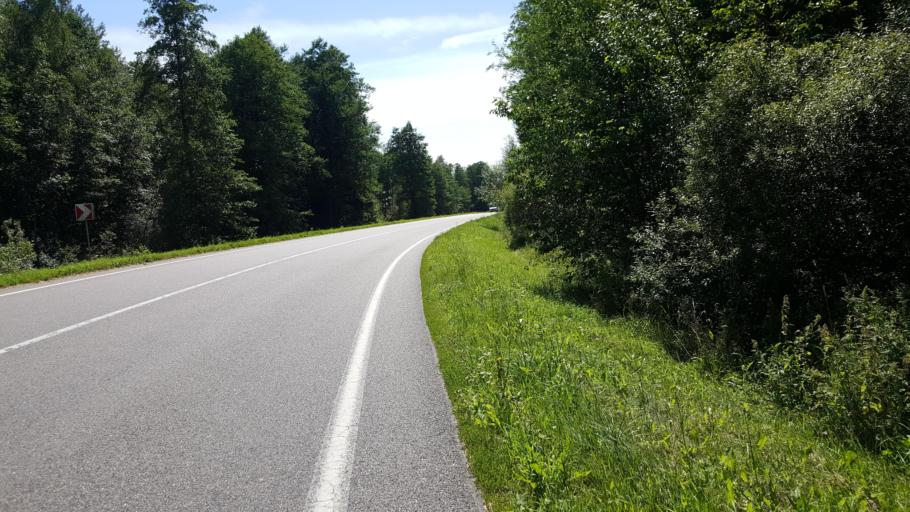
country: BY
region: Brest
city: Pruzhany
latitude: 52.4831
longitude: 24.1663
